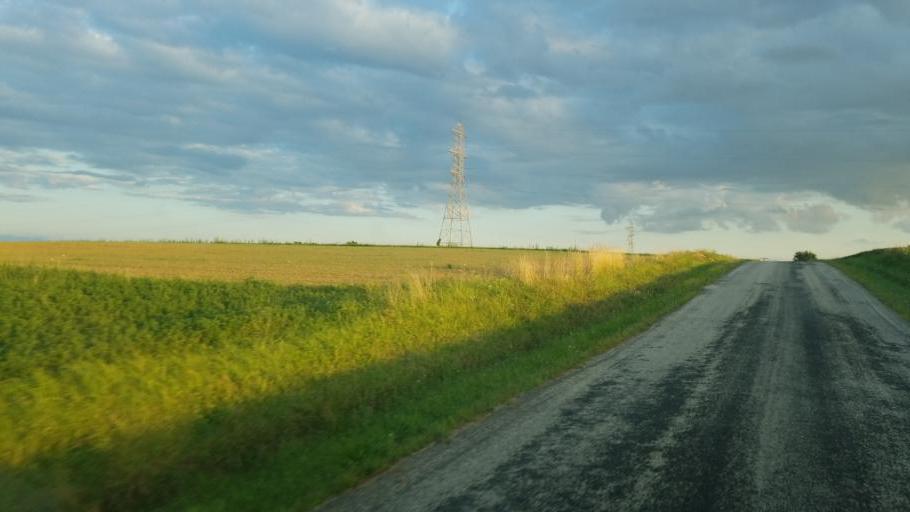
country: US
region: Ohio
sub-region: Richland County
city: Lincoln Heights
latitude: 40.8547
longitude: -82.5328
